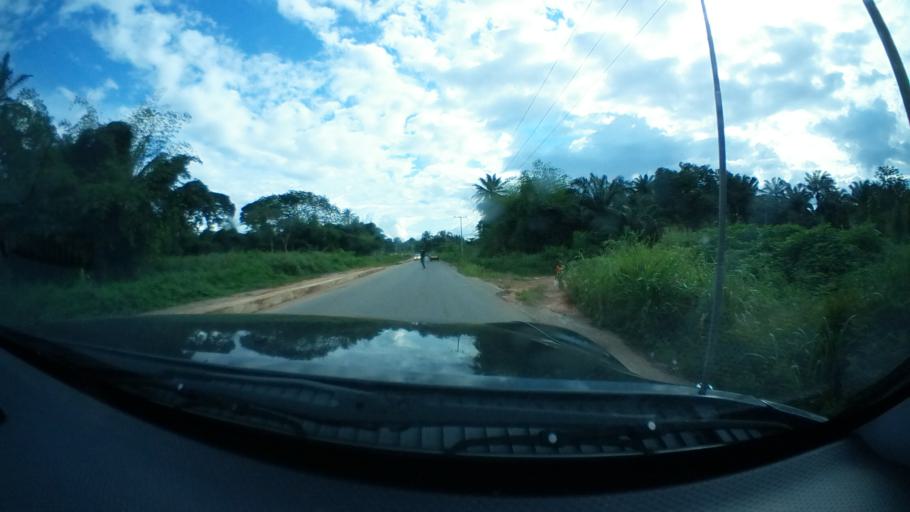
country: NG
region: Anambra
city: Uga
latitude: 5.8717
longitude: 7.1018
